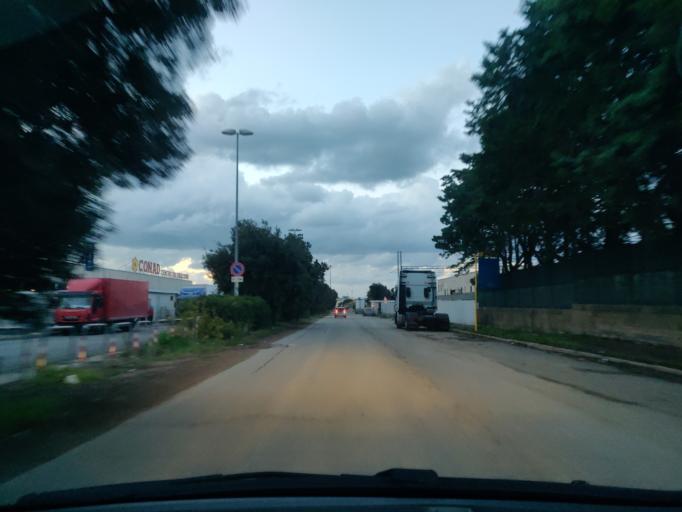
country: IT
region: Latium
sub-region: Citta metropolitana di Roma Capitale
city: Aurelia
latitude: 42.1183
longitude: 11.7786
